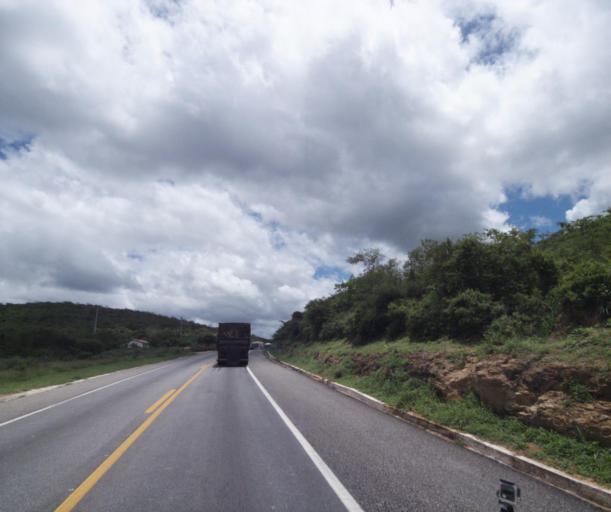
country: BR
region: Bahia
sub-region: Pocoes
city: Pocoes
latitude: -14.3675
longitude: -40.3451
